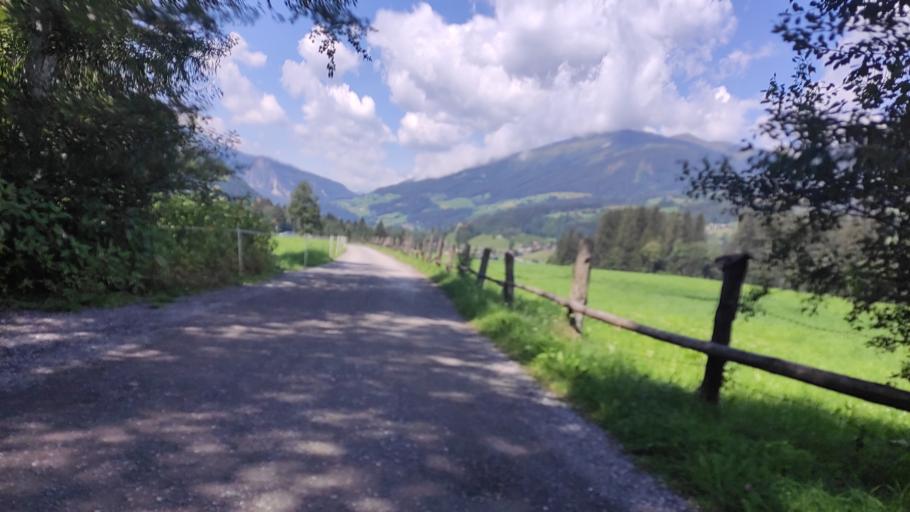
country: AT
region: Salzburg
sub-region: Politischer Bezirk Zell am See
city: Neukirchen am Grossvenediger
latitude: 47.2440
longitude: 12.2656
